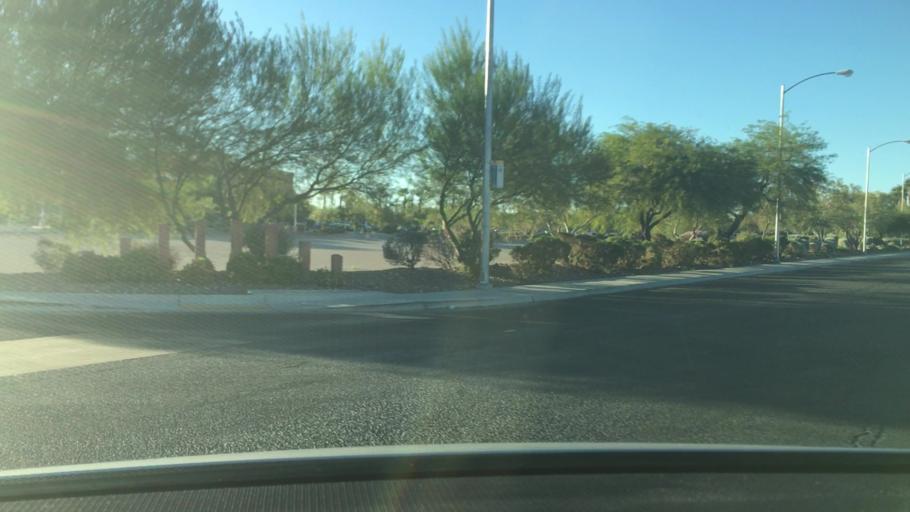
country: US
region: Nevada
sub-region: Clark County
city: Summerlin South
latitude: 36.0739
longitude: -115.2976
